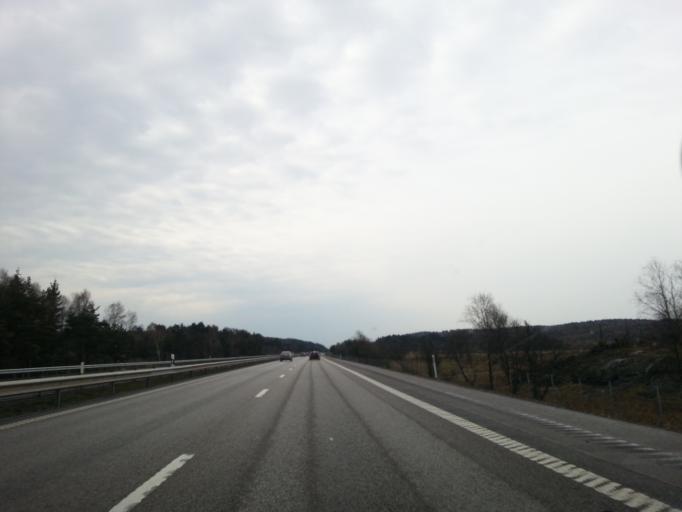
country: SE
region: Vaestra Goetaland
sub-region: Molndal
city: Lindome
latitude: 57.5460
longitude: 12.0529
